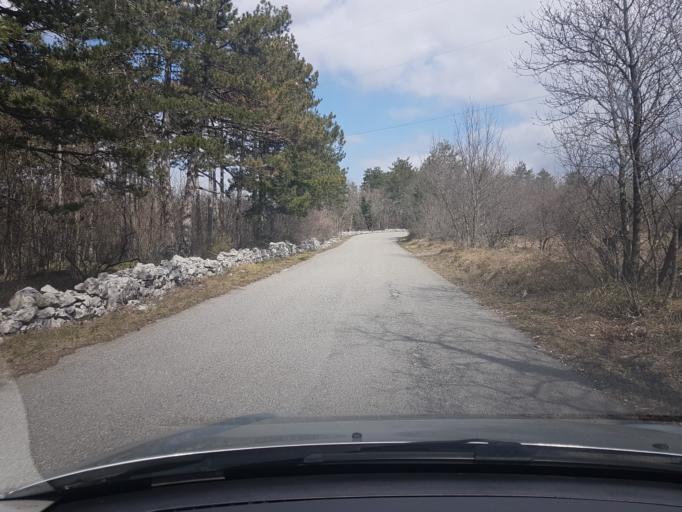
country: IT
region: Friuli Venezia Giulia
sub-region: Provincia di Trieste
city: Santa Croce
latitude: 45.7444
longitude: 13.7118
